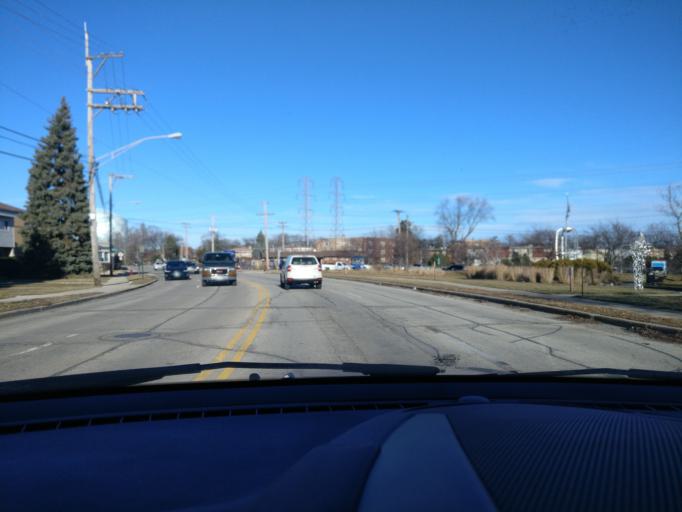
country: US
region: Illinois
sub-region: Cook County
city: Skokie
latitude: 42.0425
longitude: -87.7546
